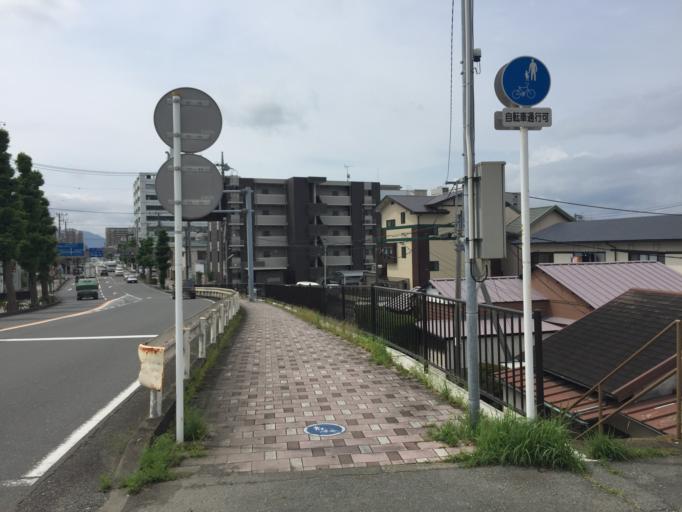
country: JP
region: Shizuoka
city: Numazu
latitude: 35.0977
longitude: 138.8631
